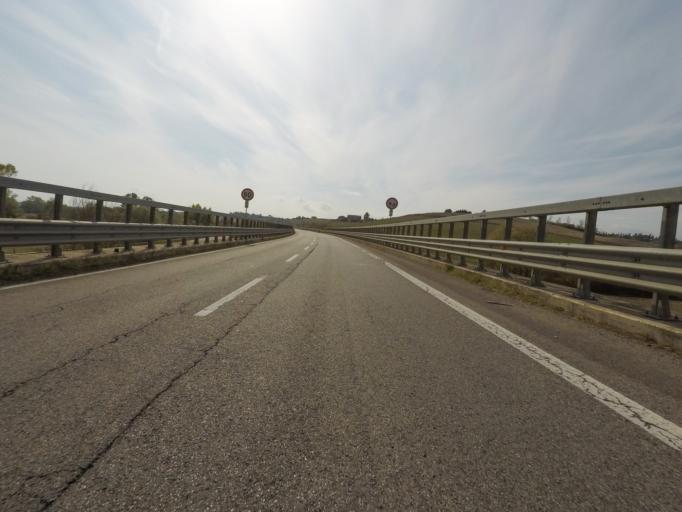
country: IT
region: Tuscany
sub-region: Provincia di Siena
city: Siena
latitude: 43.2846
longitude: 11.3322
